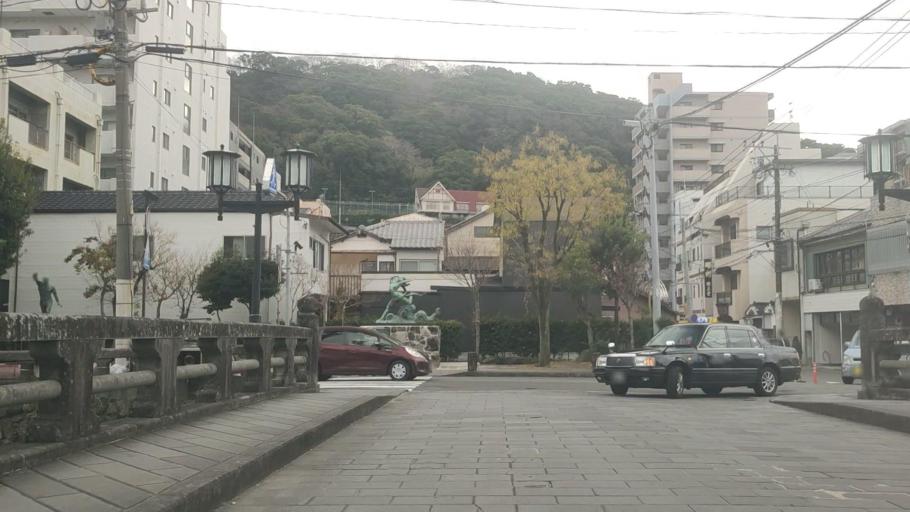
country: JP
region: Nagasaki
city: Nagasaki-shi
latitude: 32.7485
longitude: 129.8819
